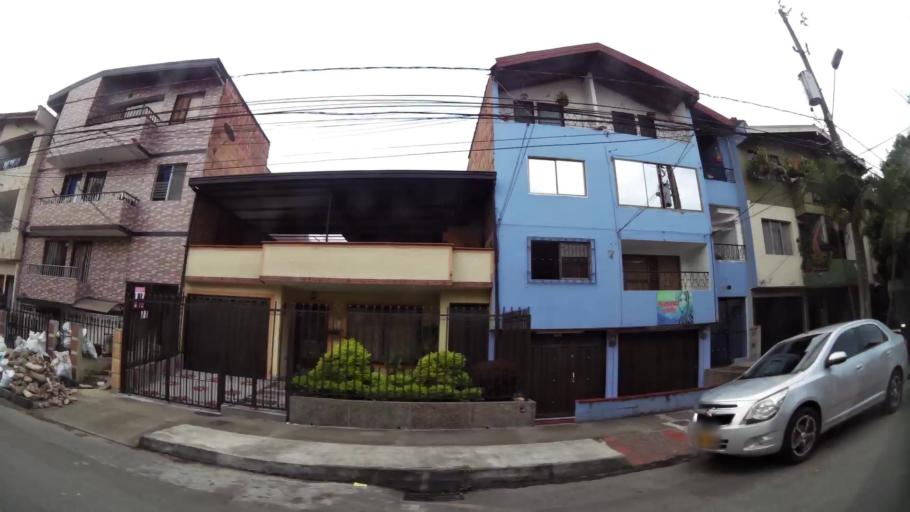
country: CO
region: Antioquia
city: Medellin
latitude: 6.2236
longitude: -75.5874
